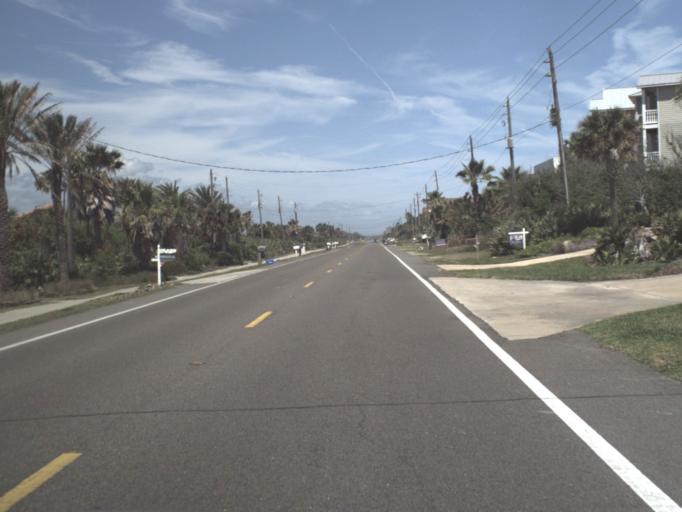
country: US
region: Florida
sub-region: Flagler County
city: Palm Coast
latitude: 29.5394
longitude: -81.1568
